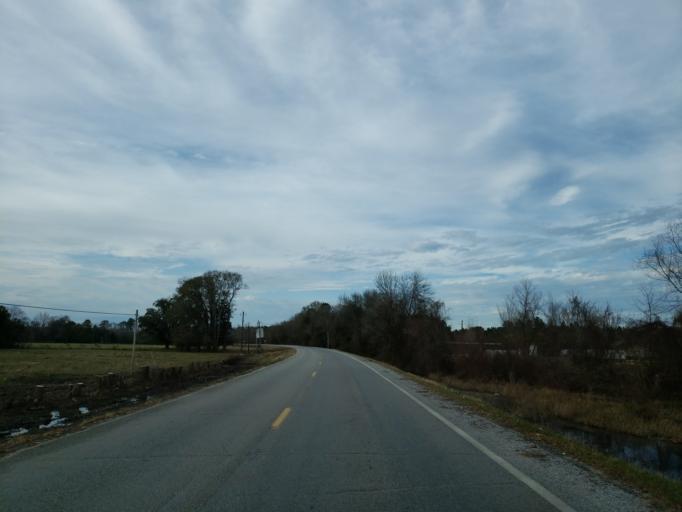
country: US
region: Mississippi
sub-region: Clarke County
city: Quitman
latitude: 31.8694
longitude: -88.7027
